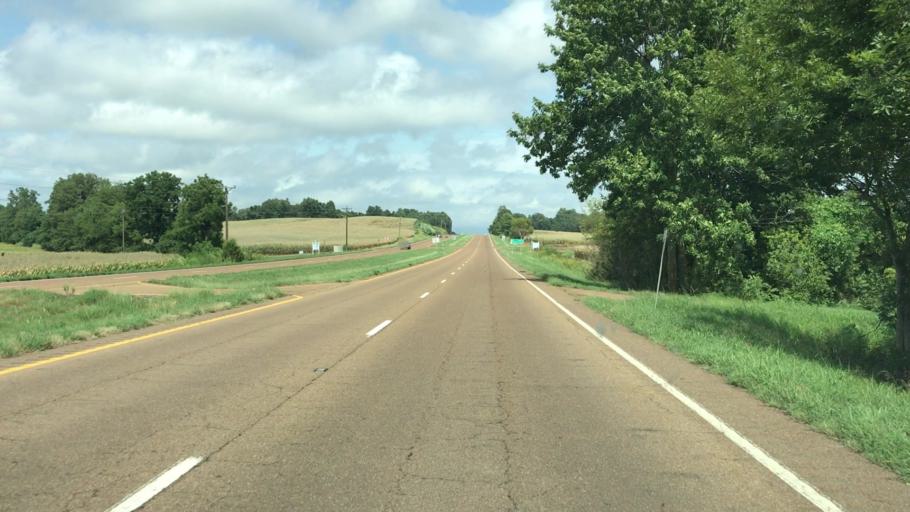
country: US
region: Tennessee
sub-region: Obion County
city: Englewood
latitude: 36.3672
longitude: -89.1263
